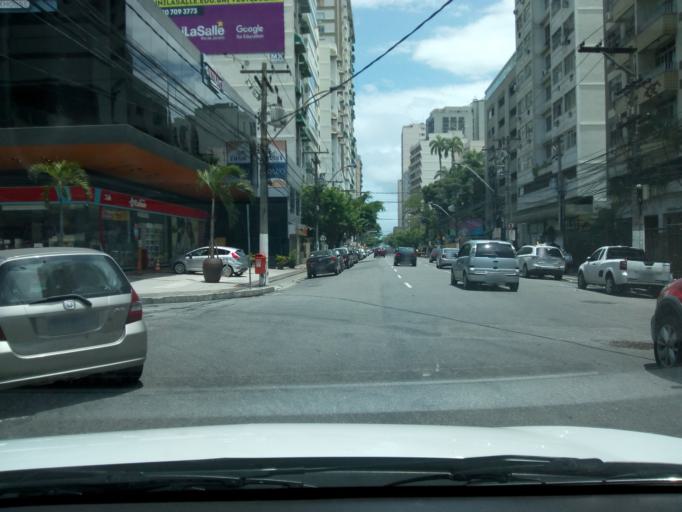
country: BR
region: Rio de Janeiro
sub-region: Niteroi
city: Niteroi
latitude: -22.9009
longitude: -43.1130
